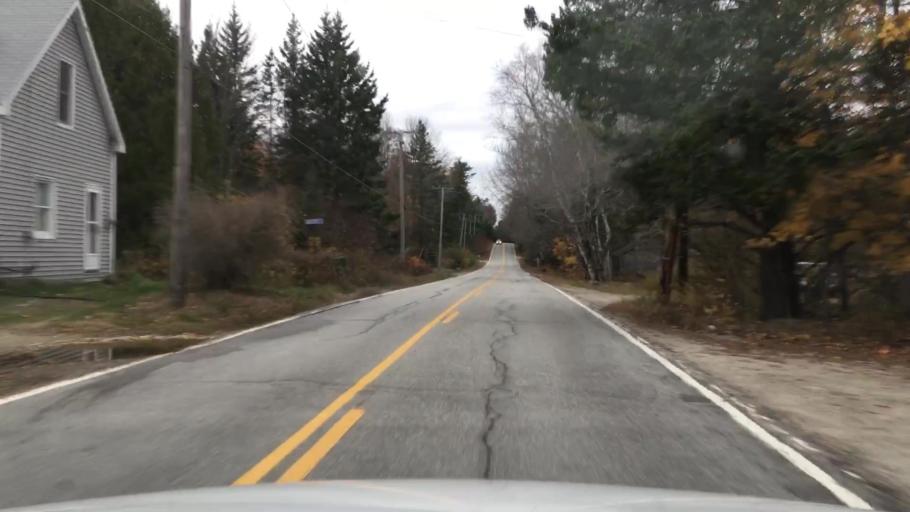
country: US
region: Maine
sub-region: Hancock County
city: Sedgwick
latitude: 44.3166
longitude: -68.5706
